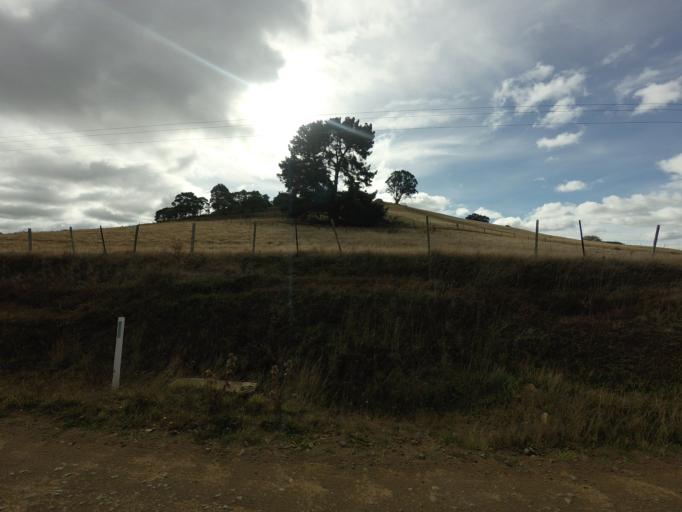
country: AU
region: Tasmania
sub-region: Sorell
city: Sorell
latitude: -42.4301
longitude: 147.4621
